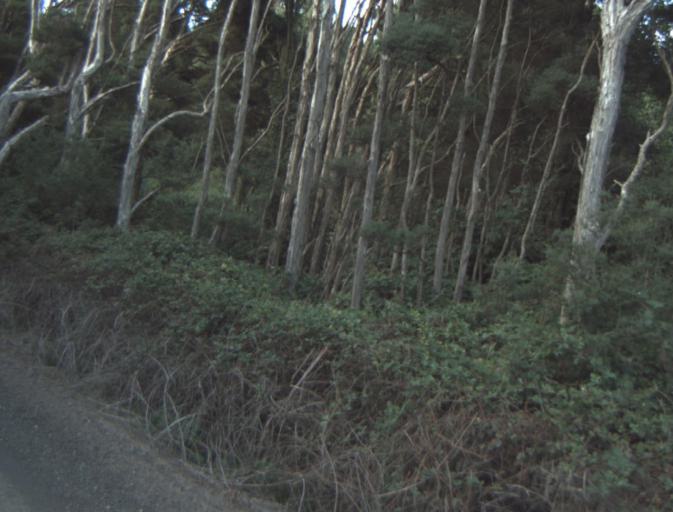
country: AU
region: Tasmania
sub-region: Launceston
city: Mayfield
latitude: -41.2740
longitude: 147.1842
